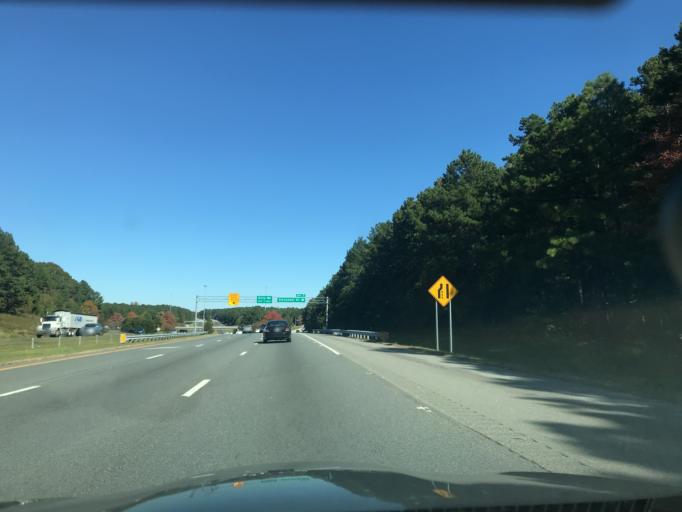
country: US
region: North Carolina
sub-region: Durham County
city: Durham
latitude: 35.9191
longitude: -78.8615
